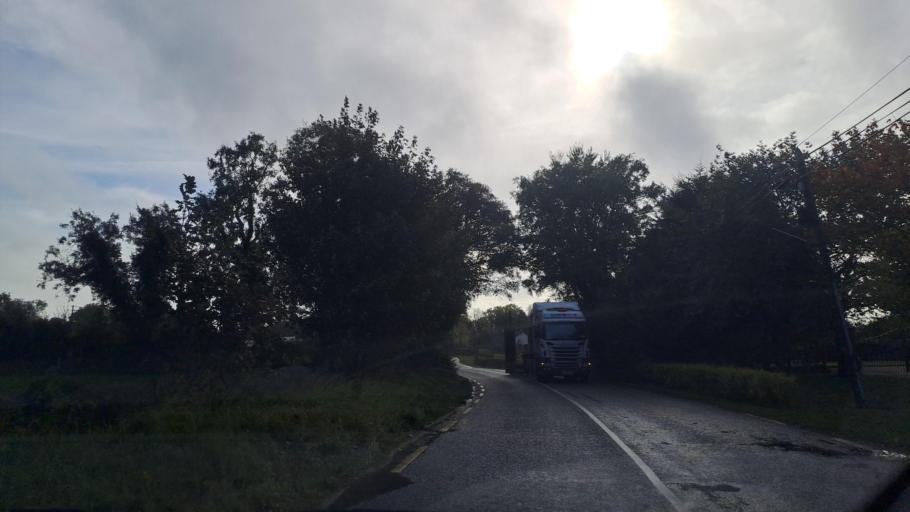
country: IE
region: Ulster
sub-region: County Monaghan
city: Carrickmacross
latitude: 53.9409
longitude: -6.7173
